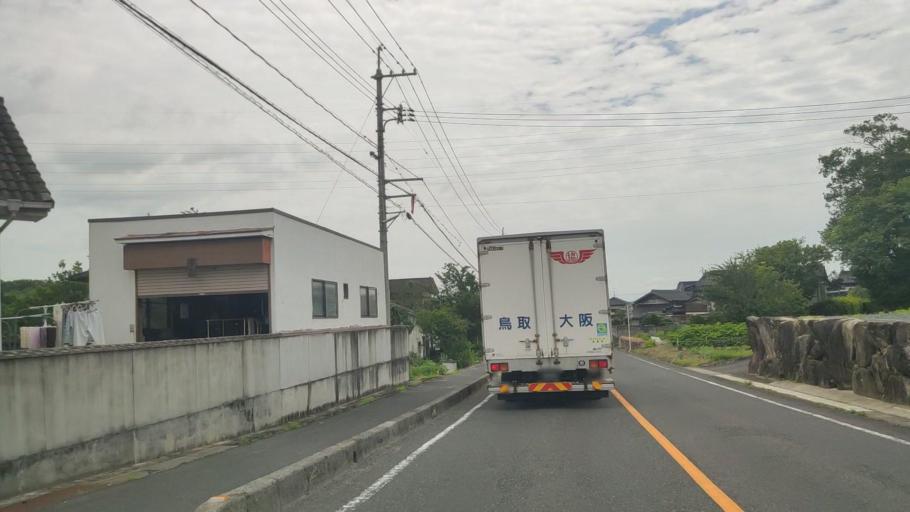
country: JP
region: Okayama
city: Tsuyama
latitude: 35.0766
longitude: 134.0860
